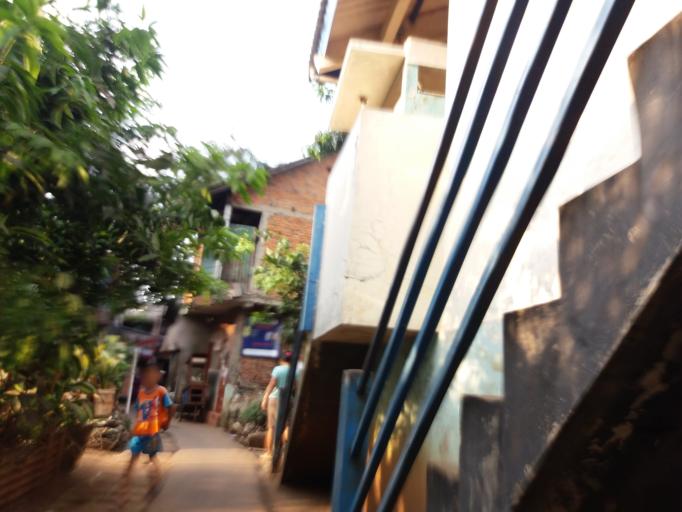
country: ID
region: Jakarta Raya
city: Jakarta
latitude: -6.2451
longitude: 106.8136
